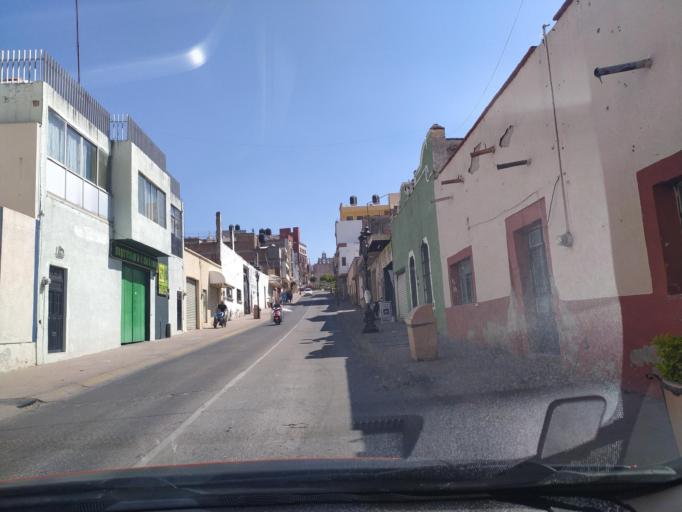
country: MX
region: Jalisco
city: San Juan de los Lagos
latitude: 21.2485
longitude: -102.3316
